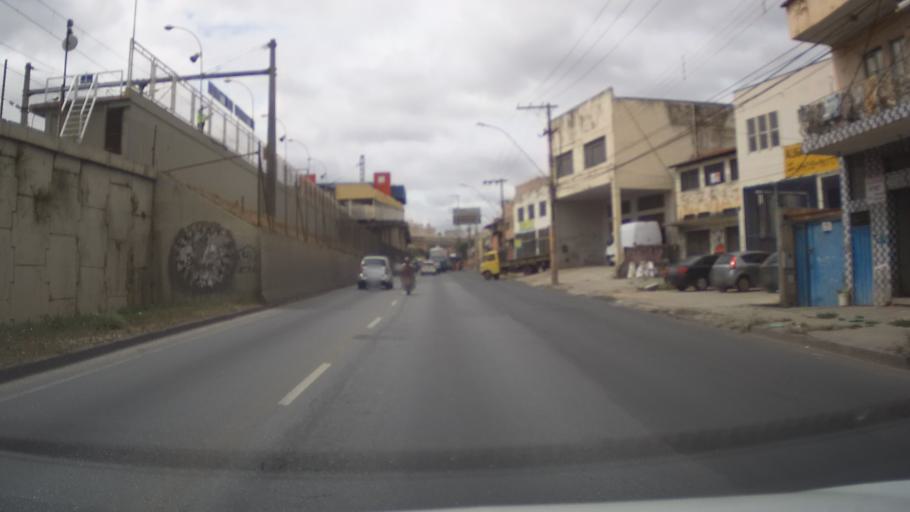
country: BR
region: Minas Gerais
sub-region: Belo Horizonte
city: Belo Horizonte
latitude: -19.8330
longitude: -43.9406
